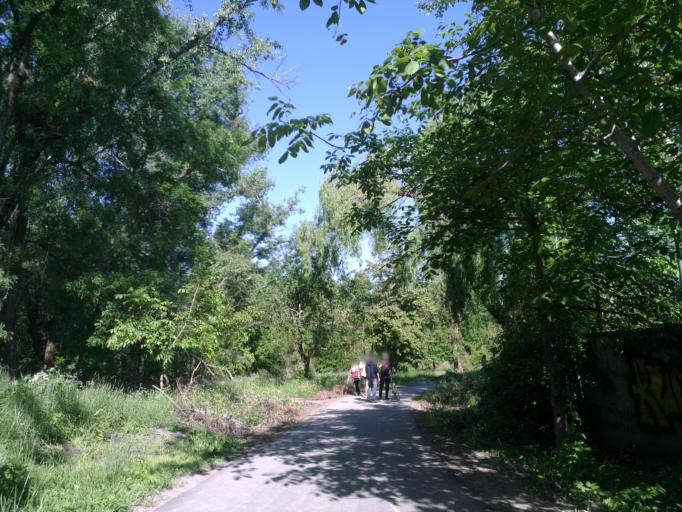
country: MD
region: Chisinau
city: Chisinau
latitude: 47.0154
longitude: 28.8074
